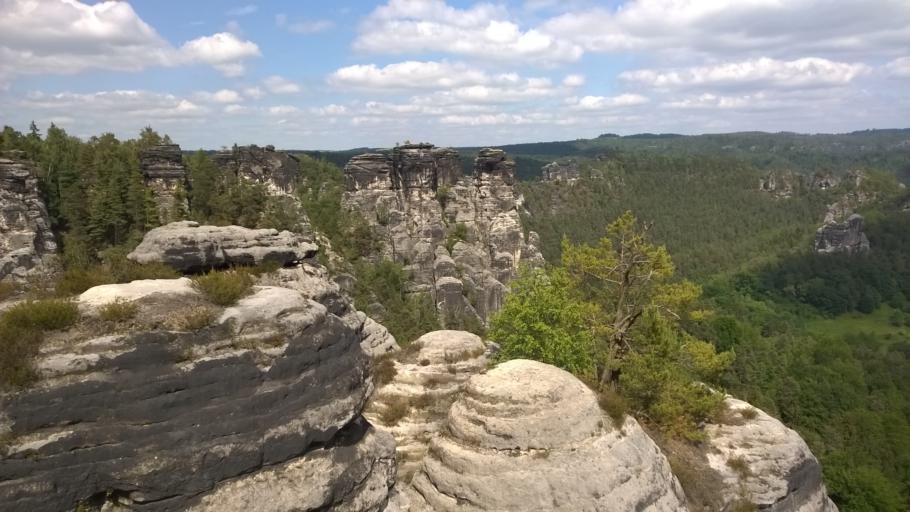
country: DE
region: Saxony
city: Stadt Wehlen
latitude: 50.9629
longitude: 14.0730
